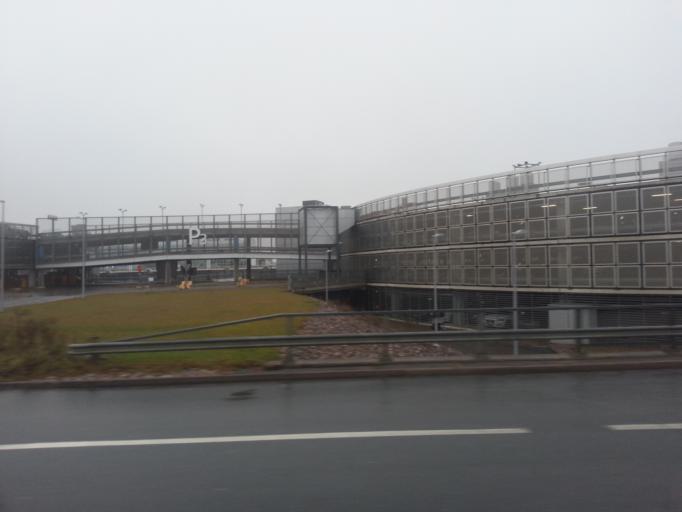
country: FI
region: Uusimaa
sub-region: Helsinki
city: Vantaa
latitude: 60.3141
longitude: 24.9693
